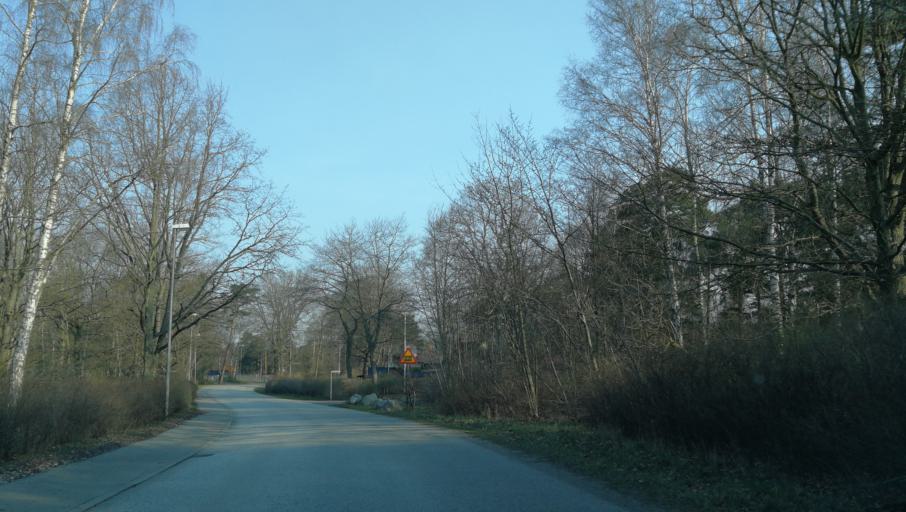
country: SE
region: Skane
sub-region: Ystads Kommun
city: Ystad
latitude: 55.4283
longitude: 13.8489
